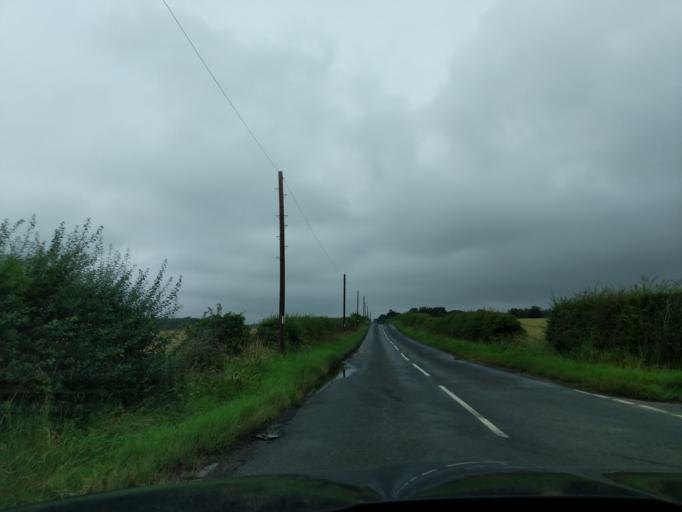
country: GB
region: England
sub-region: Northumberland
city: Ford
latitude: 55.6662
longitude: -2.1018
